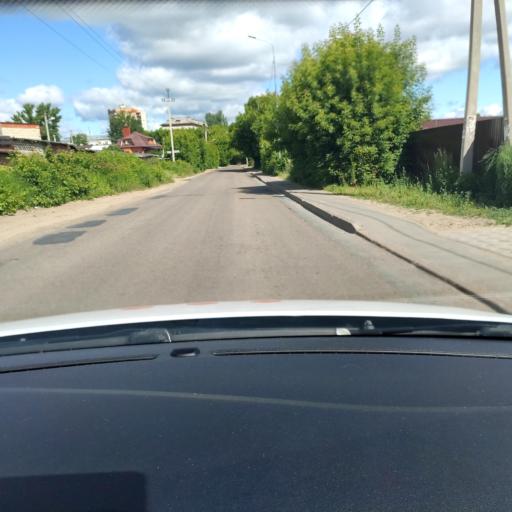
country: RU
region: Tatarstan
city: Vysokaya Gora
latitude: 55.8649
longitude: 49.2364
